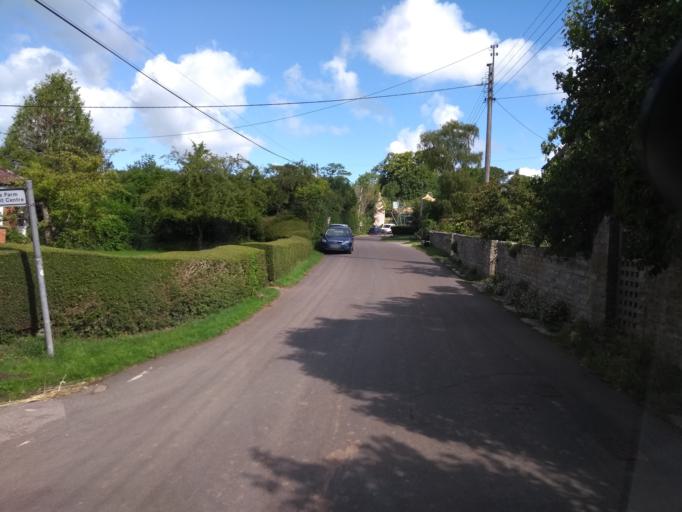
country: GB
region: England
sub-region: Somerset
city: Street
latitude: 51.0879
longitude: -2.7441
